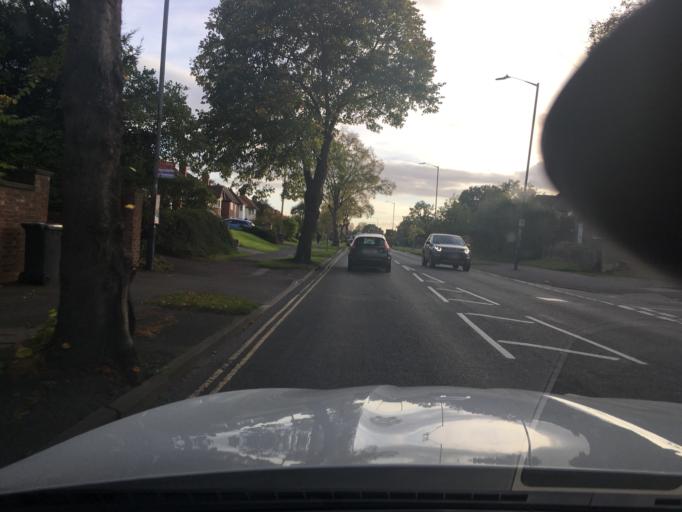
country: GB
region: England
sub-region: Warwickshire
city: Warwick
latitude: 52.2763
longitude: -1.5940
